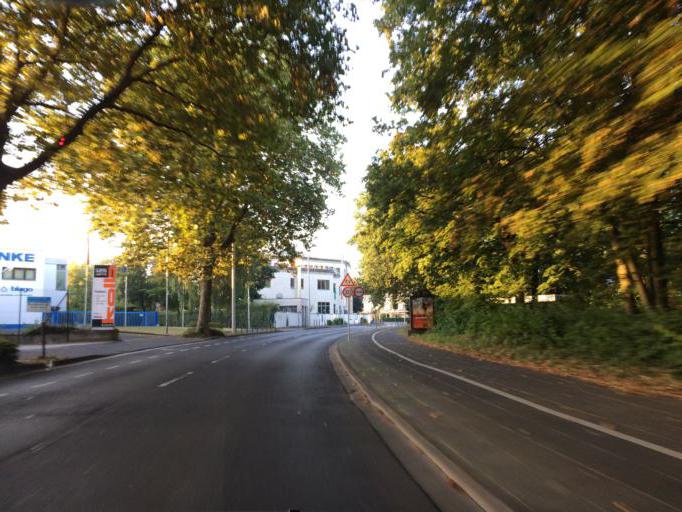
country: DE
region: North Rhine-Westphalia
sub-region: Regierungsbezirk Koln
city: Konigswinter
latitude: 50.6680
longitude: 7.1748
